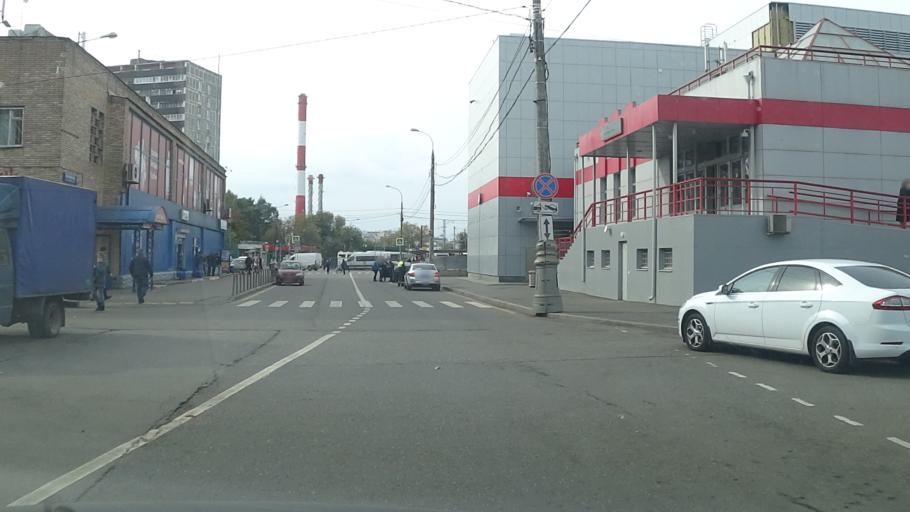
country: RU
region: Moscow
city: Solntsevo
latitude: 55.6568
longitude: 37.3854
